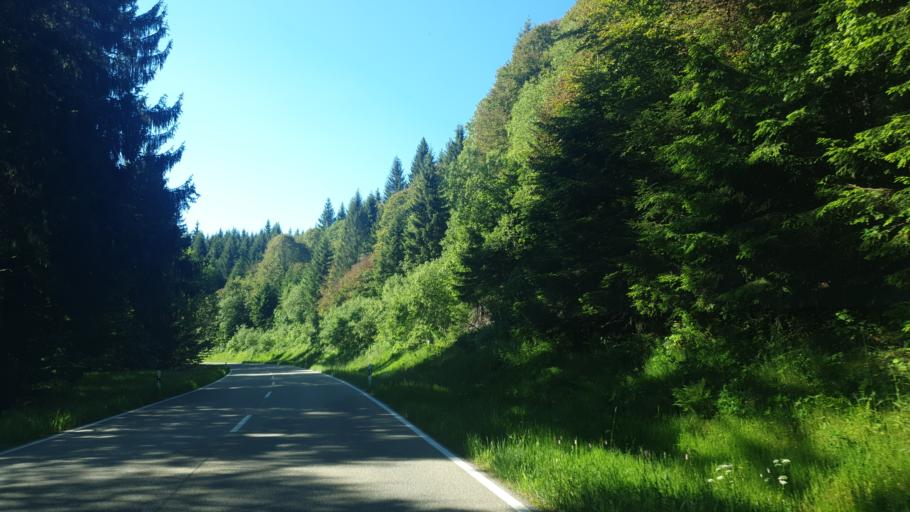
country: DE
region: Baden-Wuerttemberg
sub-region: Freiburg Region
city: Wieden
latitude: 47.8814
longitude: 7.9010
